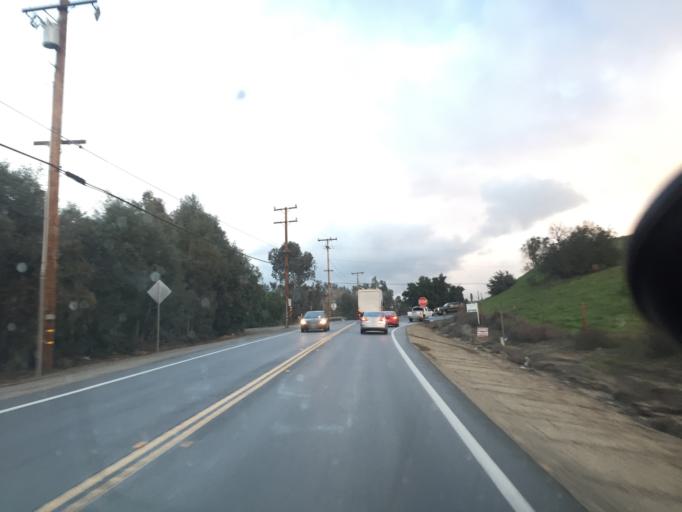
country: US
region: California
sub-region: San Bernardino County
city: Redlands
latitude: 33.9930
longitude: -117.1547
